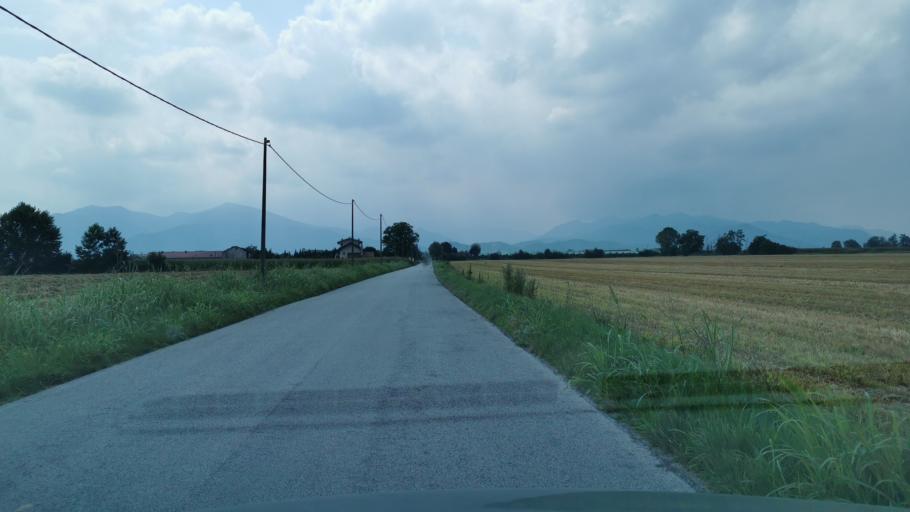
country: IT
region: Piedmont
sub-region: Provincia di Cuneo
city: San Rocco
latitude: 44.4293
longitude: 7.4790
